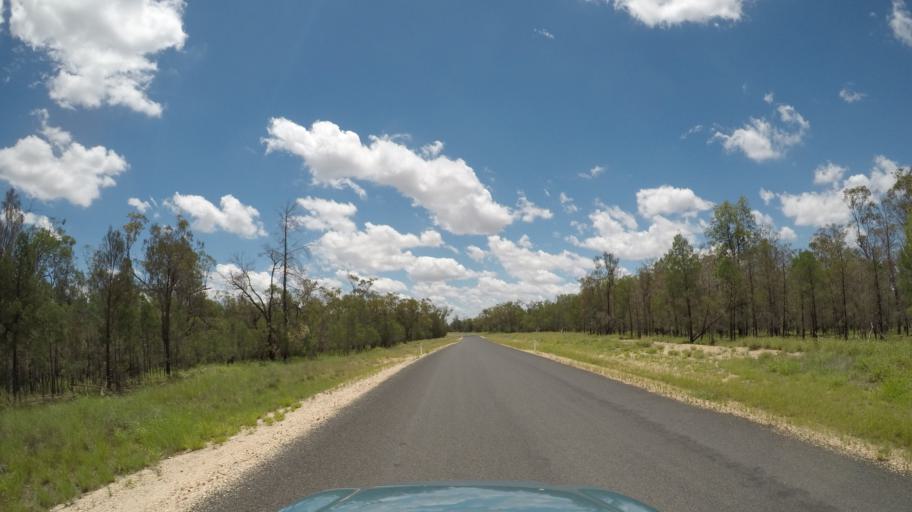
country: AU
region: Queensland
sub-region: Goondiwindi
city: Goondiwindi
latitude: -28.1562
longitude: 150.1210
